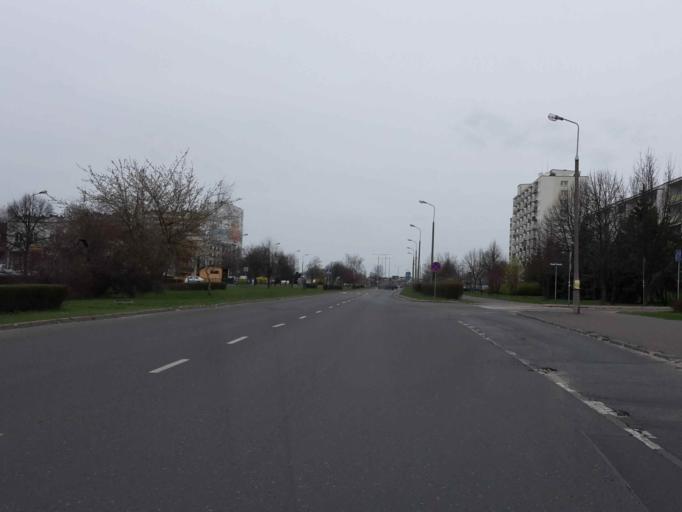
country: PL
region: Kujawsko-Pomorskie
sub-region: Powiat torunski
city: Lubicz Dolny
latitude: 53.0233
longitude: 18.6891
